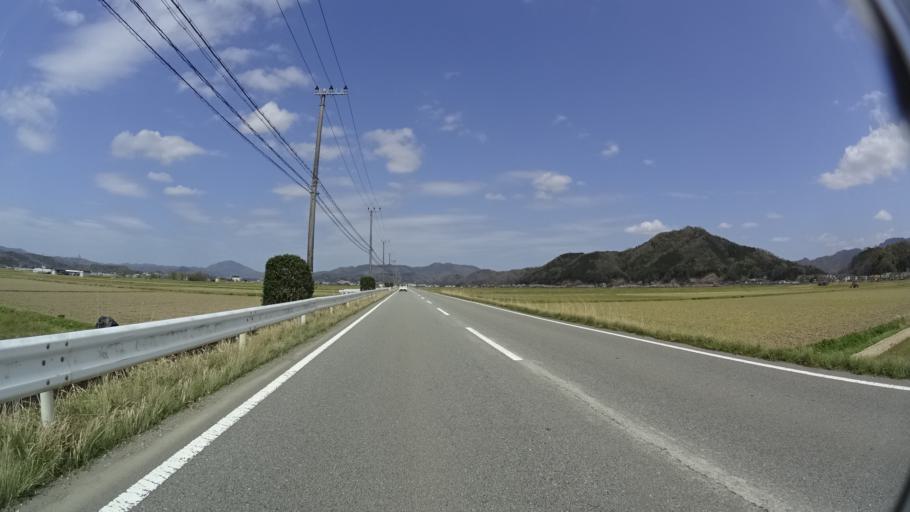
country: JP
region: Hyogo
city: Toyooka
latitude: 35.5103
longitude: 134.8400
